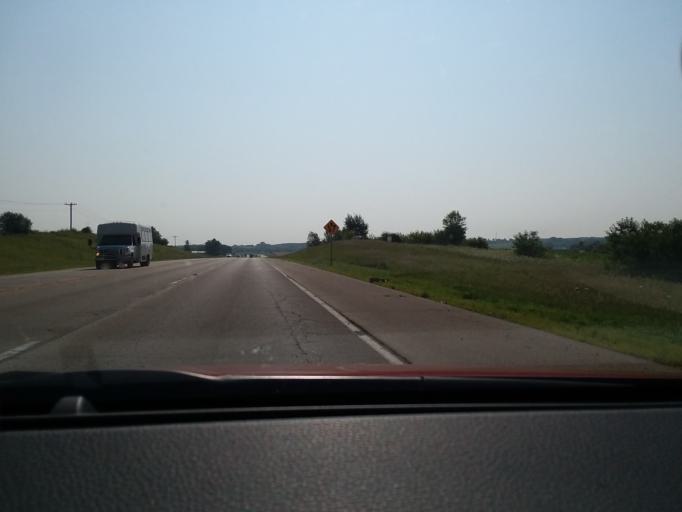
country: US
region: Wisconsin
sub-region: Dane County
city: Waunakee
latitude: 43.1919
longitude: -89.4303
